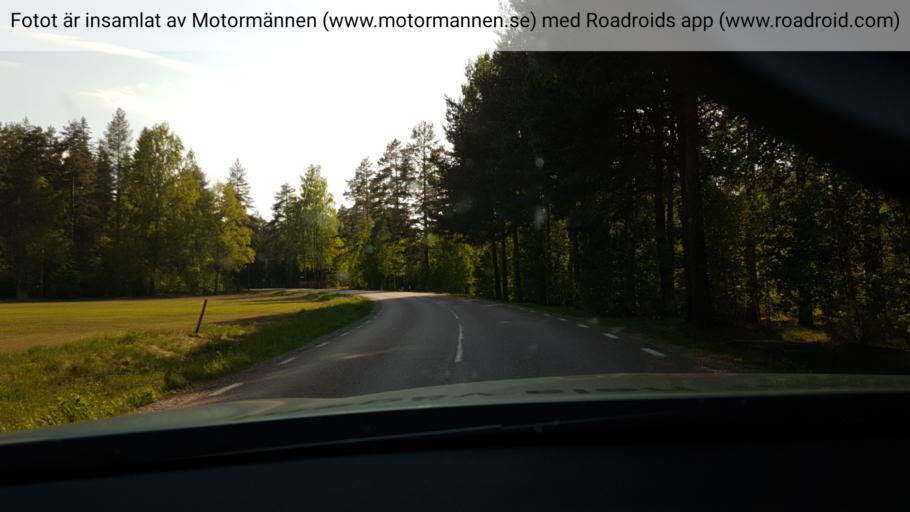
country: SE
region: Gaevleborg
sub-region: Sandvikens Kommun
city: Arsunda
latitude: 60.4504
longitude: 16.6956
